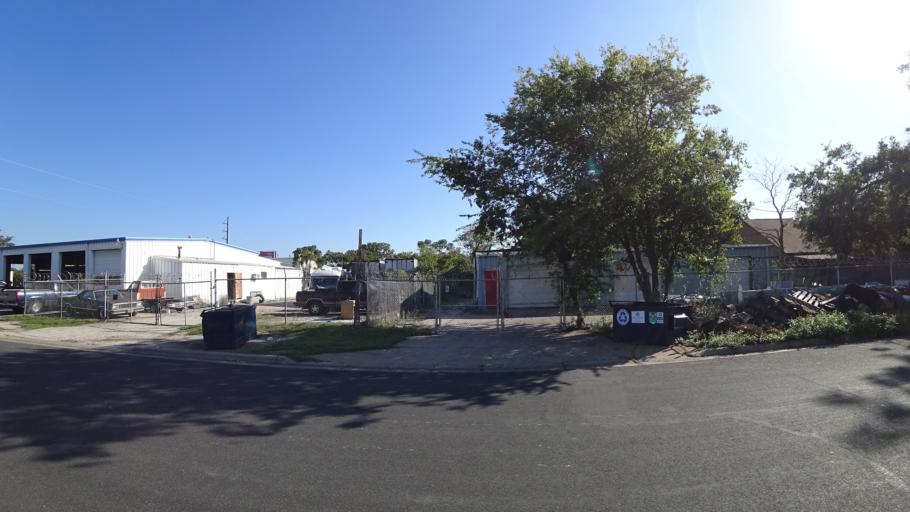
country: US
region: Texas
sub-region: Travis County
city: Wells Branch
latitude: 30.3560
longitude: -97.7008
